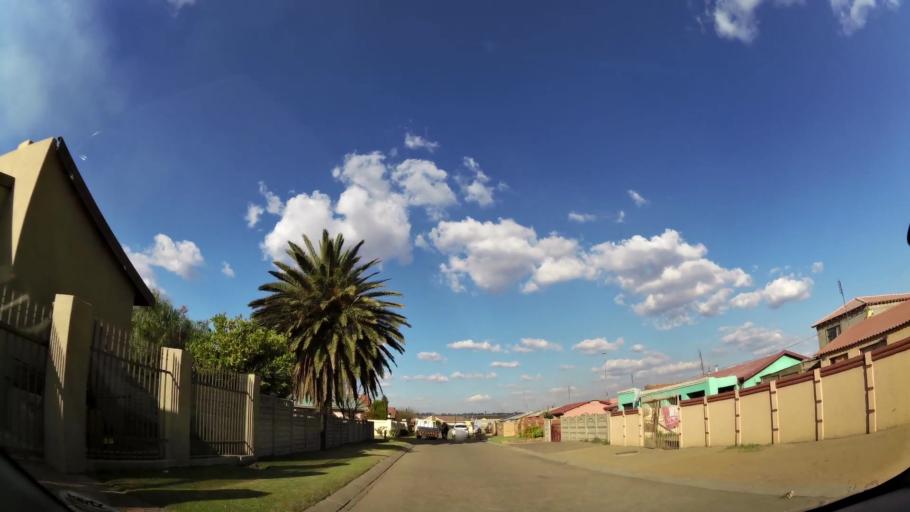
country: ZA
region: Mpumalanga
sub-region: Nkangala District Municipality
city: Witbank
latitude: -25.8716
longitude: 29.1810
